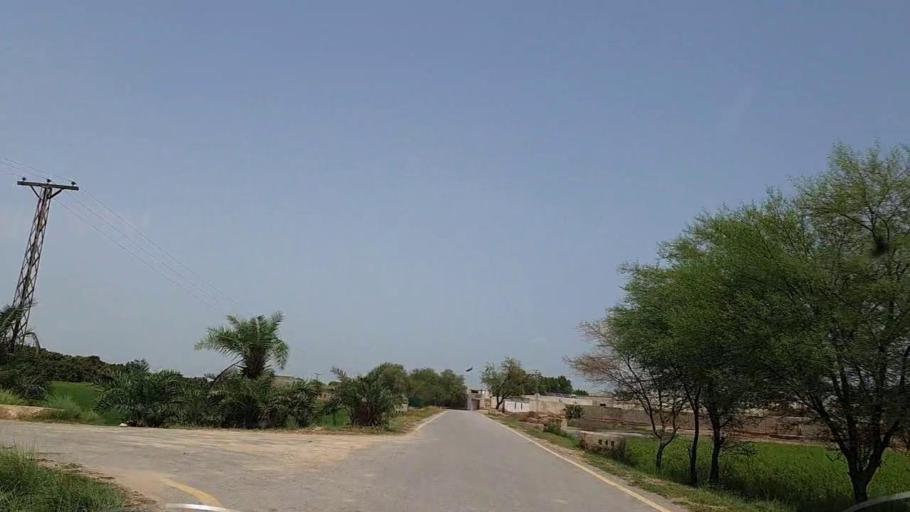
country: PK
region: Sindh
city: Tharu Shah
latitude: 26.9904
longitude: 68.0834
